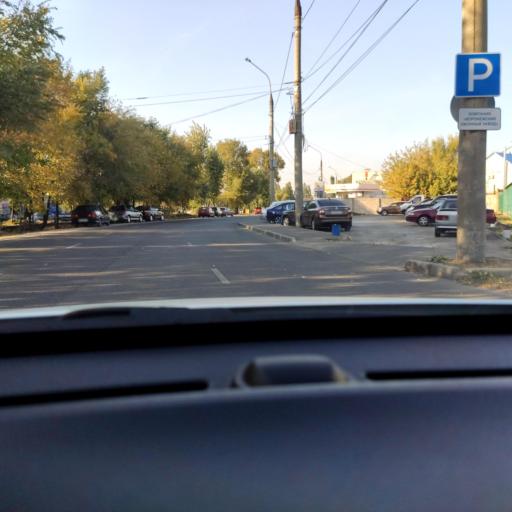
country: RU
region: Voronezj
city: Voronezh
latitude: 51.6789
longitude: 39.1668
